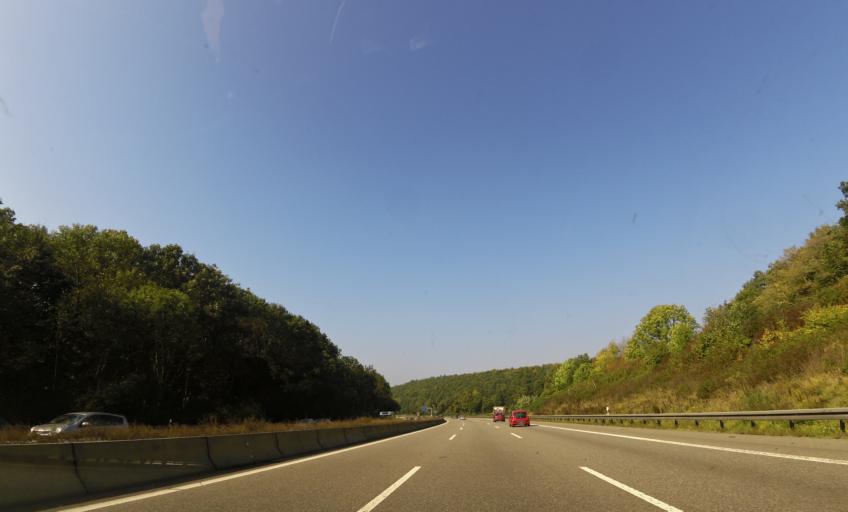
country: DE
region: Baden-Wuerttemberg
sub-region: Regierungsbezirk Stuttgart
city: Ittlingen
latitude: 49.2259
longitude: 8.9446
